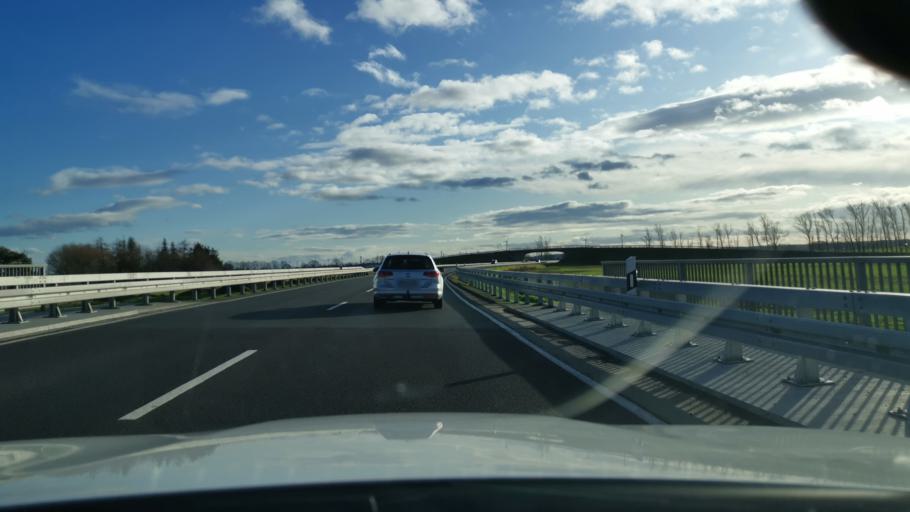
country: DE
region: Saxony-Anhalt
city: Wittenburg
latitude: 51.8231
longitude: 12.6444
